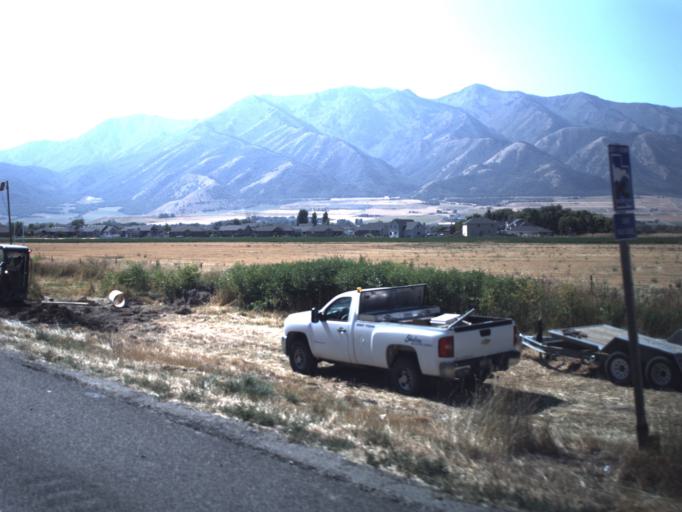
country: US
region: Utah
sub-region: Cache County
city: Wellsville
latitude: 41.6535
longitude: -111.9054
